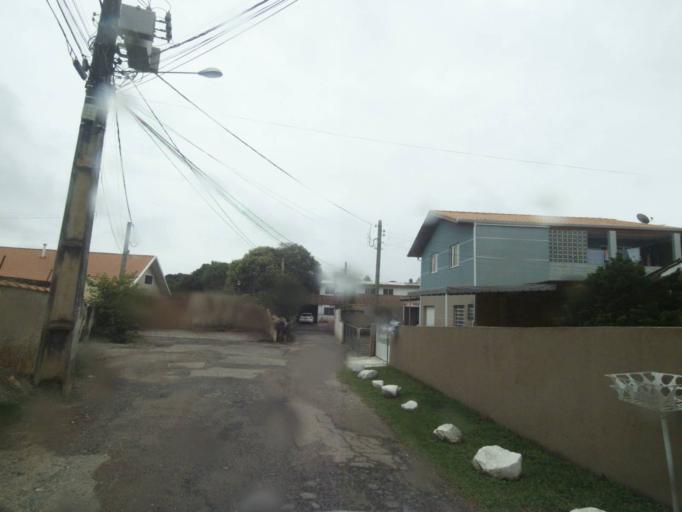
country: BR
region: Parana
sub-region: Curitiba
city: Curitiba
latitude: -25.4286
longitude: -49.3337
